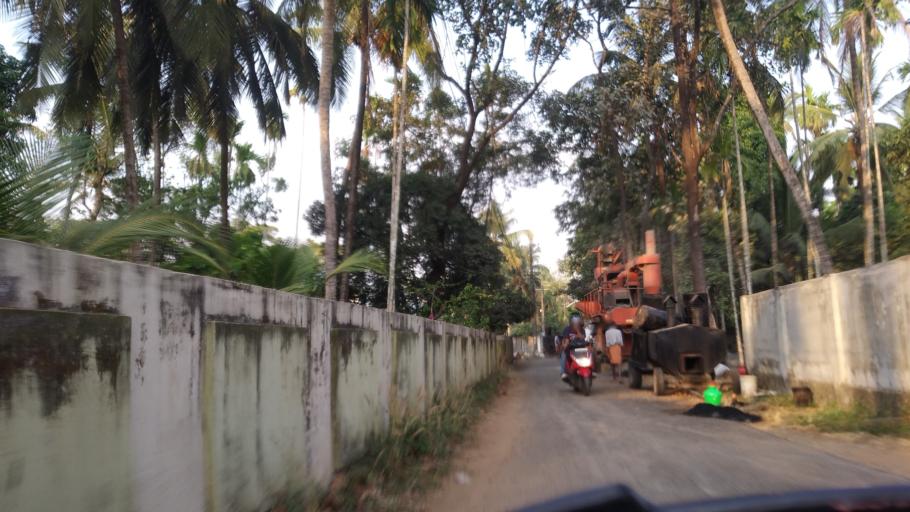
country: IN
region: Kerala
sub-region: Thrissur District
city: Thanniyam
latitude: 10.4097
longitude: 76.0926
